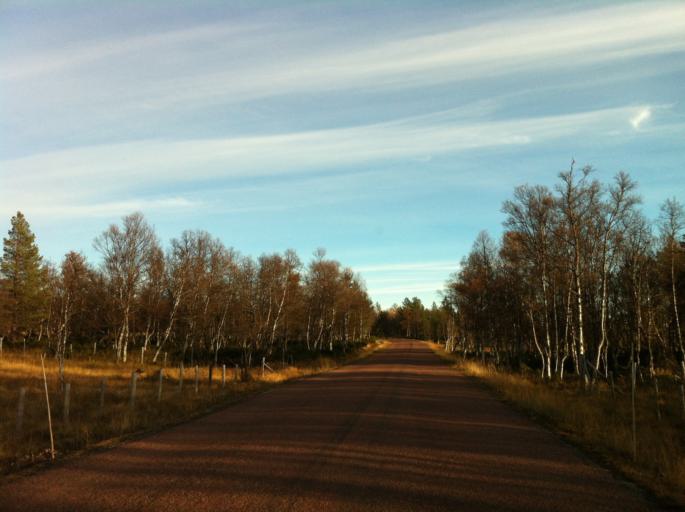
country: NO
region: Hedmark
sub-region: Engerdal
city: Engerdal
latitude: 62.0801
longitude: 12.1530
